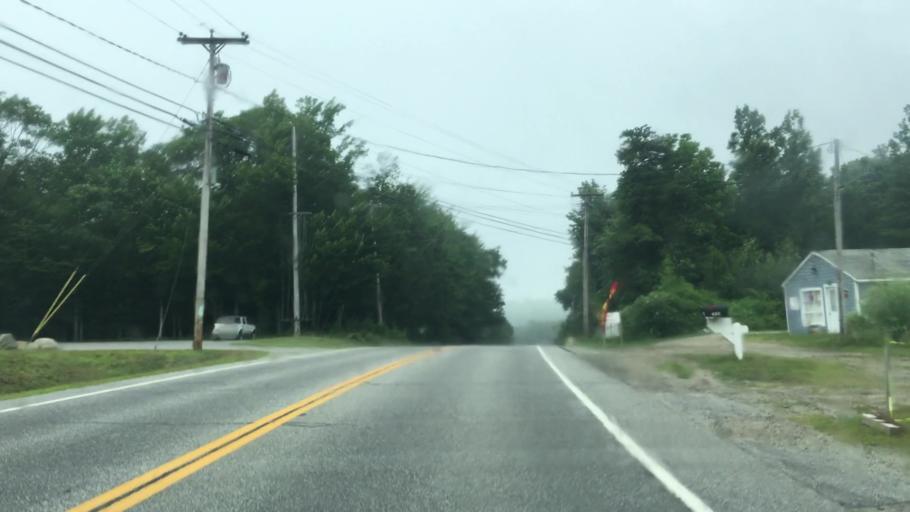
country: US
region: Maine
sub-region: Lincoln County
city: Edgecomb
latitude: 43.9728
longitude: -69.6326
